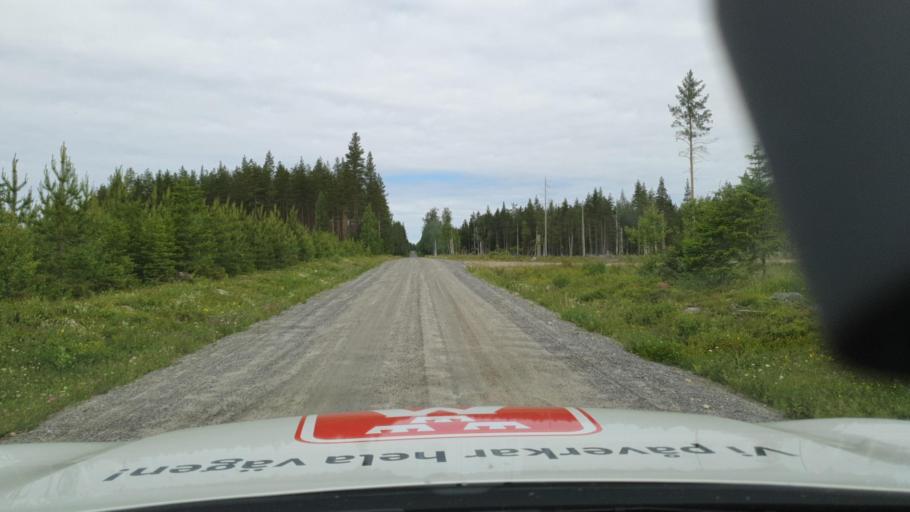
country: SE
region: Vaesterbotten
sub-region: Skelleftea Kommun
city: Burtraesk
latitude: 64.4480
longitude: 20.3033
